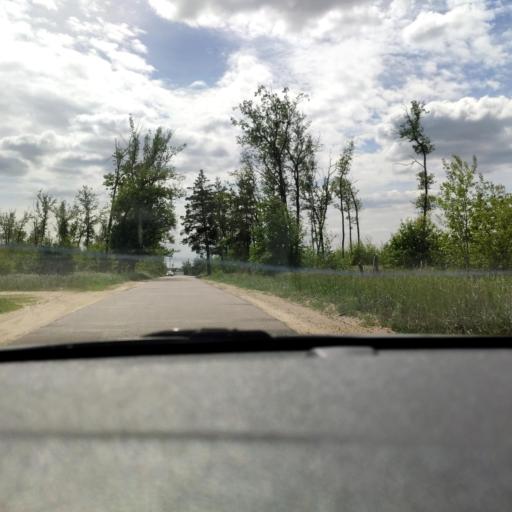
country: RU
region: Voronezj
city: Somovo
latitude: 51.7807
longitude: 39.3029
